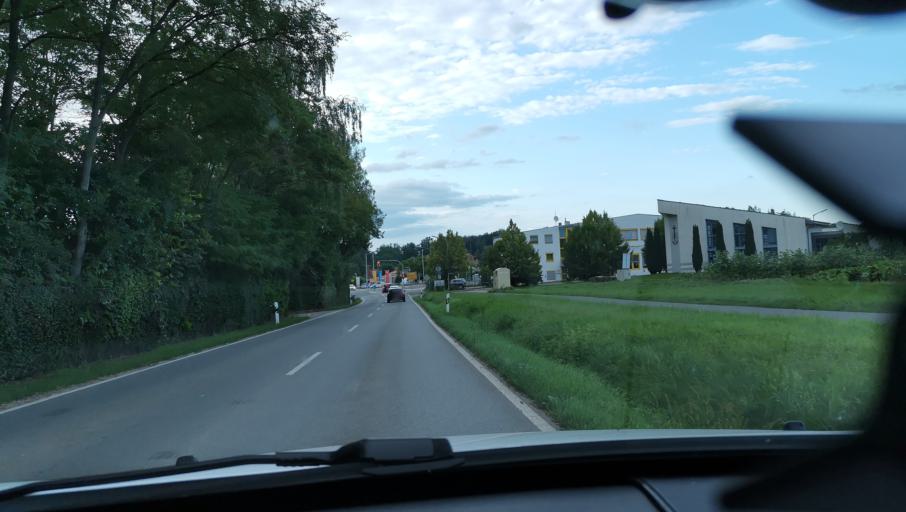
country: DE
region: Bavaria
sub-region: Regierungsbezirk Mittelfranken
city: Zirndorf
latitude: 49.4306
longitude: 10.9349
